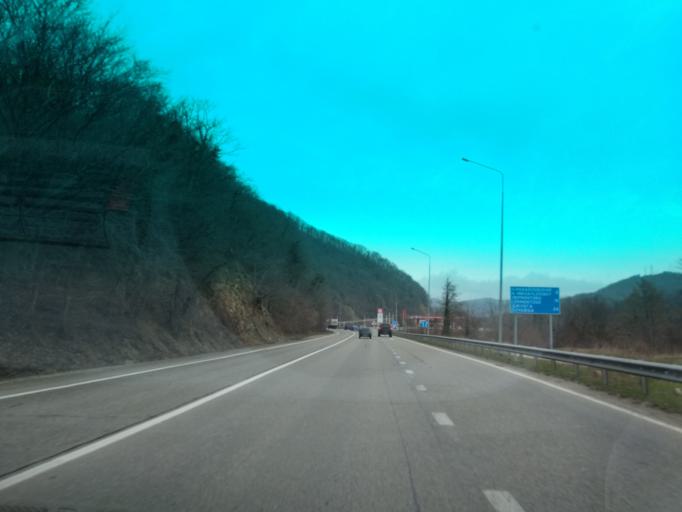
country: RU
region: Krasnodarskiy
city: Ol'ginka
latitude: 44.2152
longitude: 38.8948
